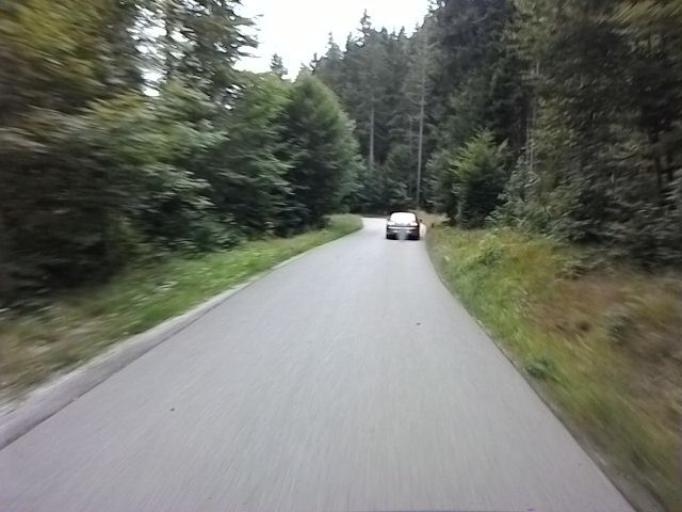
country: DE
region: Bavaria
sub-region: Upper Bavaria
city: Wallgau
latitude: 47.5359
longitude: 11.3308
